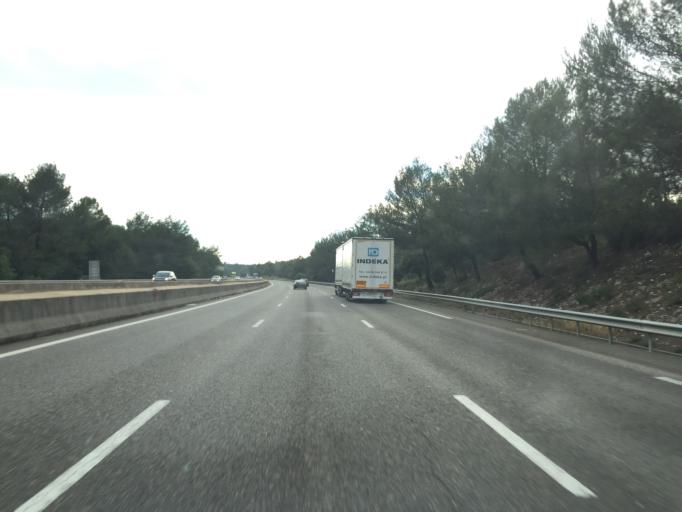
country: FR
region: Provence-Alpes-Cote d'Azur
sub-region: Departement du Var
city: Bras
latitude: 43.4251
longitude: 5.9770
